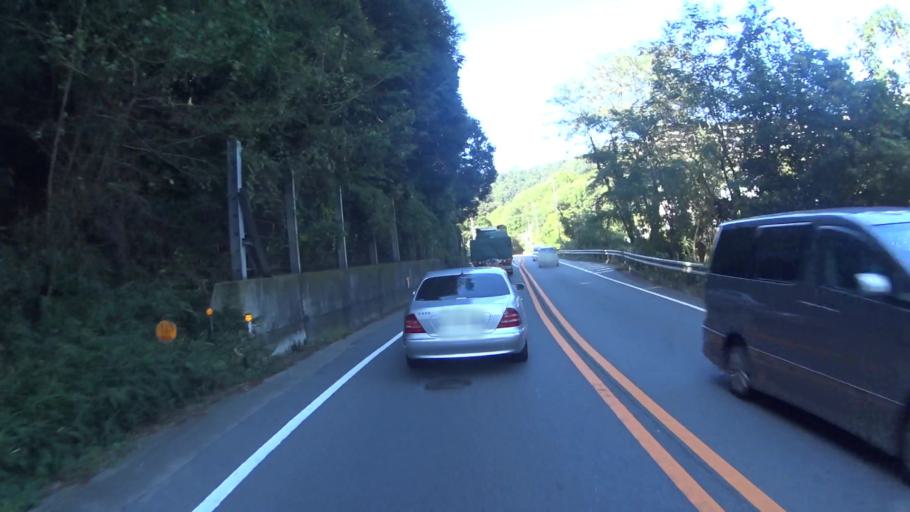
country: JP
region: Kyoto
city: Muko
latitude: 34.9805
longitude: 135.6489
